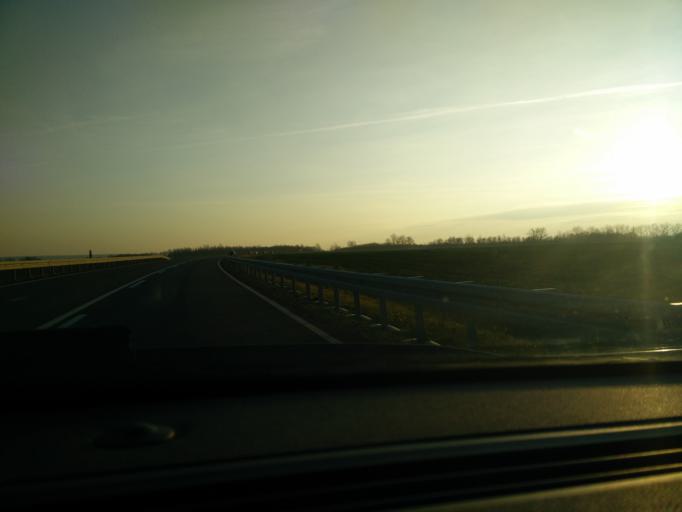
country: DE
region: Saxony
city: Grossposna
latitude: 51.2428
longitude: 12.4884
